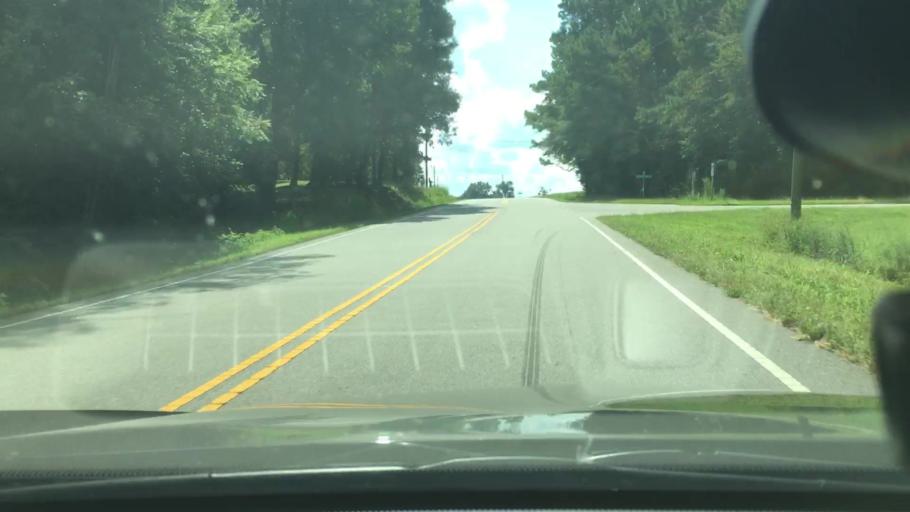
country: US
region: North Carolina
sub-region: Edgecombe County
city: Pinetops
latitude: 35.7200
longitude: -77.5291
